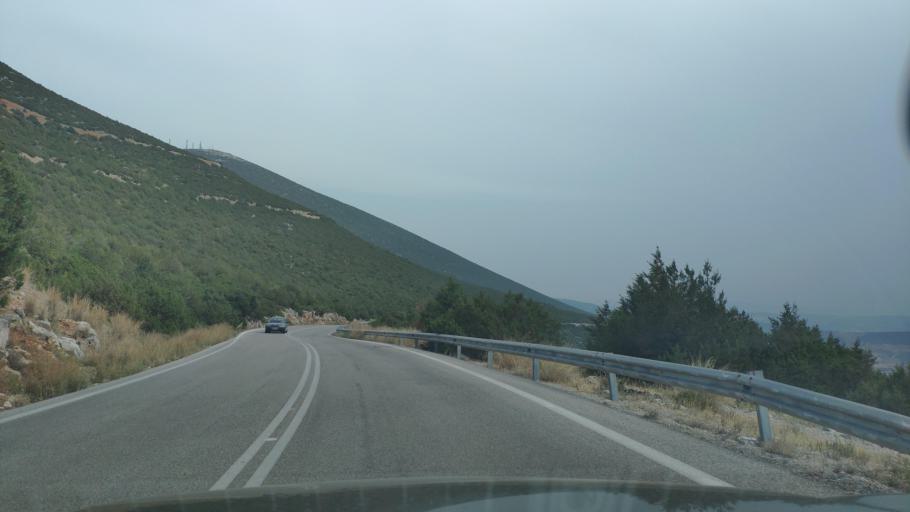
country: GR
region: Peloponnese
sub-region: Nomos Argolidos
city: Didyma
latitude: 37.4984
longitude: 23.1910
